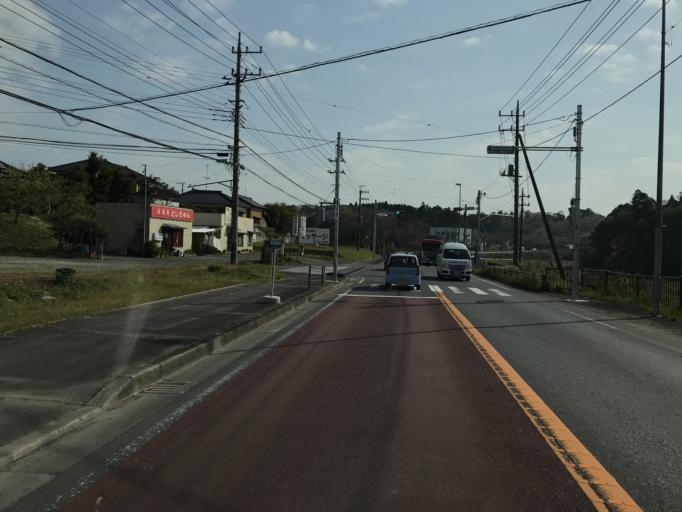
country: JP
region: Chiba
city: Narita
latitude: 35.7969
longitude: 140.3415
